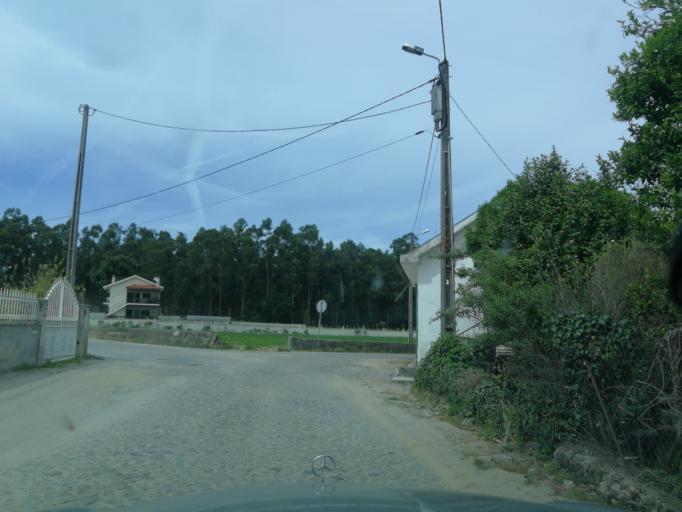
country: PT
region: Braga
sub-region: Braga
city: Oliveira
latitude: 41.4723
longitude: -8.4799
